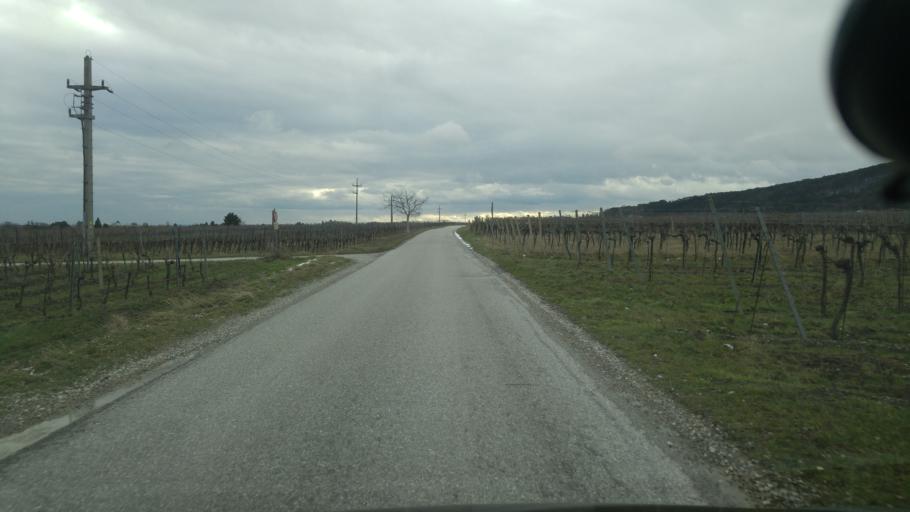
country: AT
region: Lower Austria
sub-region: Politischer Bezirk Baden
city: Bad Voslau
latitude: 47.9832
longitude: 16.2083
